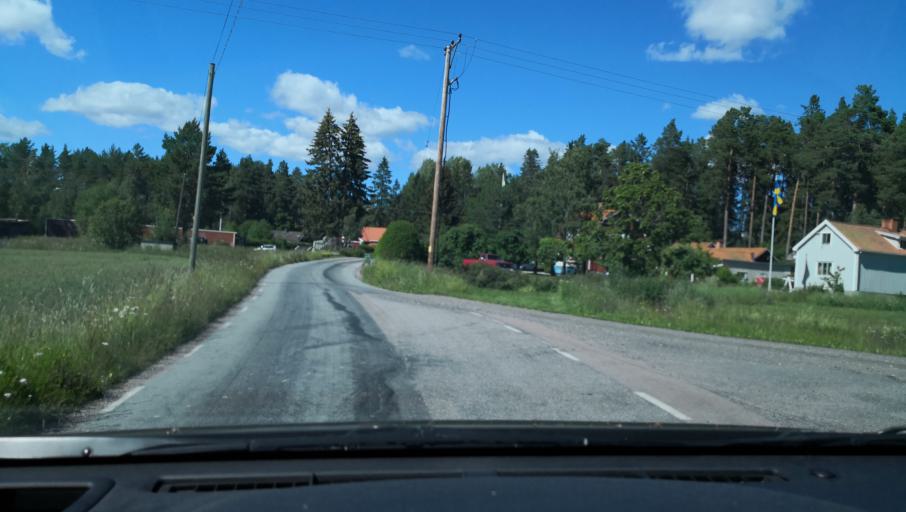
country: SE
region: Soedermanland
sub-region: Eskilstuna Kommun
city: Hallbybrunn
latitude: 59.3095
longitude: 16.3747
